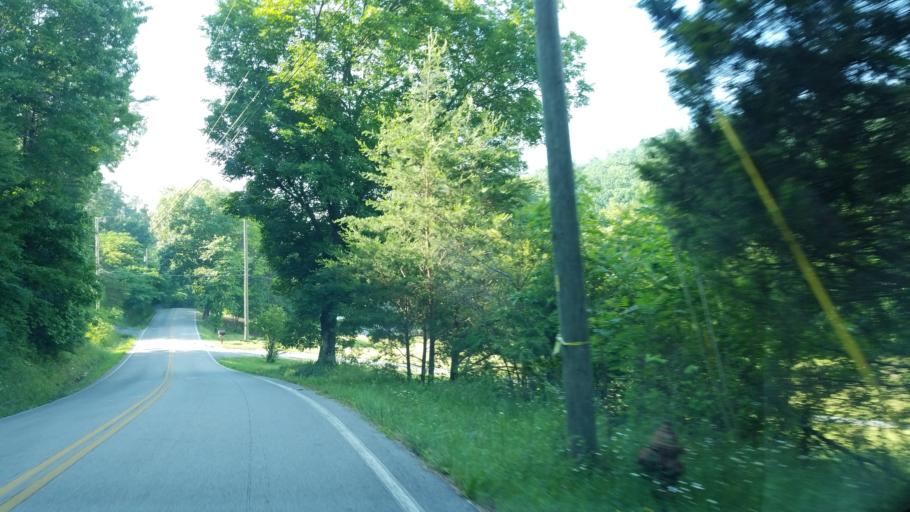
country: US
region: Tennessee
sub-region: Hamilton County
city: Collegedale
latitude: 35.0859
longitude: -85.0114
